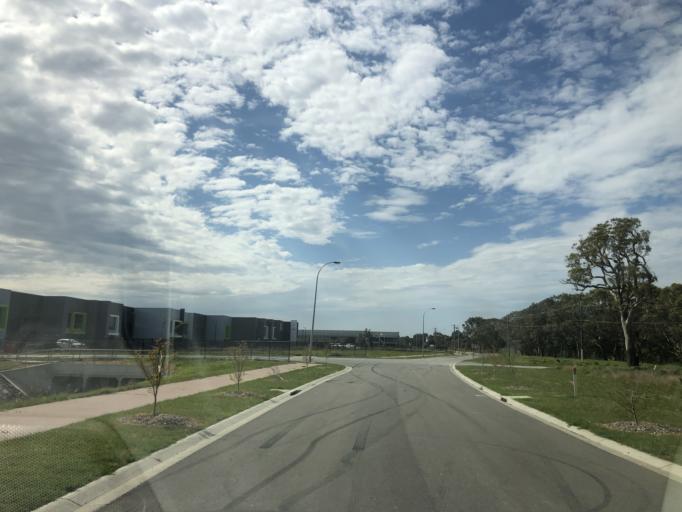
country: AU
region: Victoria
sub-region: Casey
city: Hampton Park
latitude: -38.0441
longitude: 145.2265
